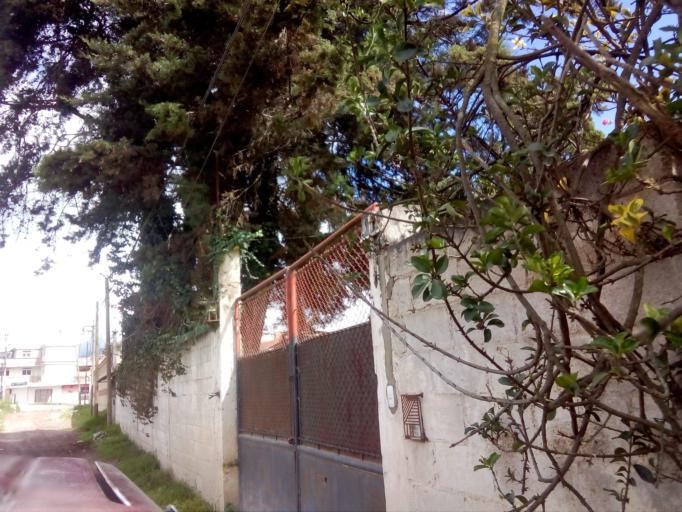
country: GT
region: Quetzaltenango
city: Quetzaltenango
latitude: 14.8486
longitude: -91.5114
